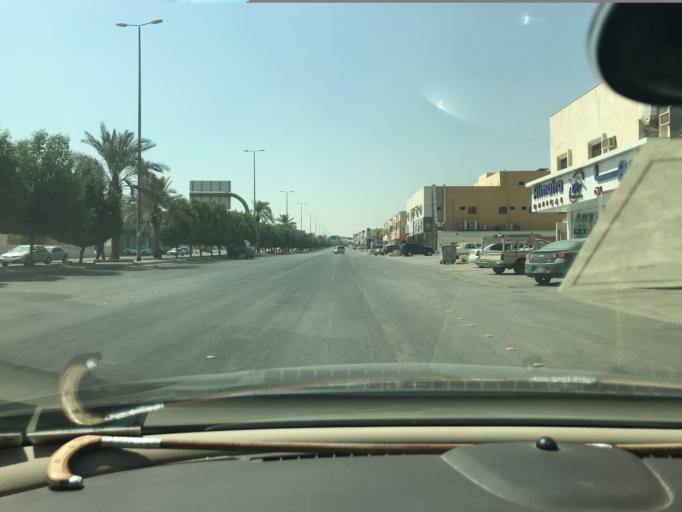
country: SA
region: Ar Riyad
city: Riyadh
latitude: 24.7059
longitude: 46.7839
